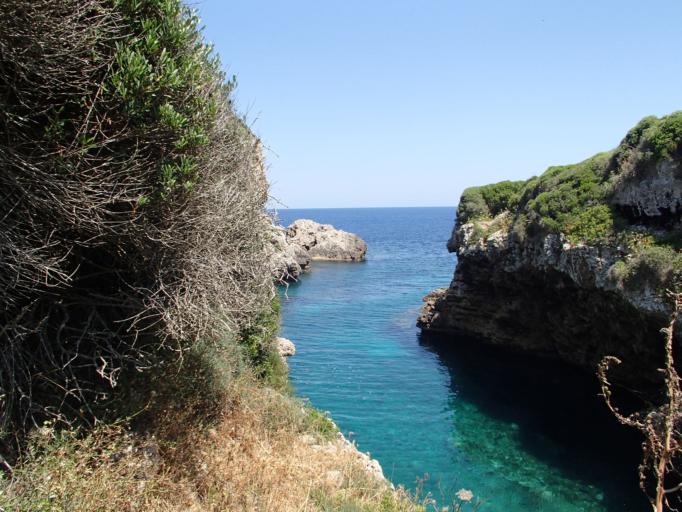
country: ES
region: Balearic Islands
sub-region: Illes Balears
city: Es Castell
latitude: 39.8411
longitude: 4.2985
